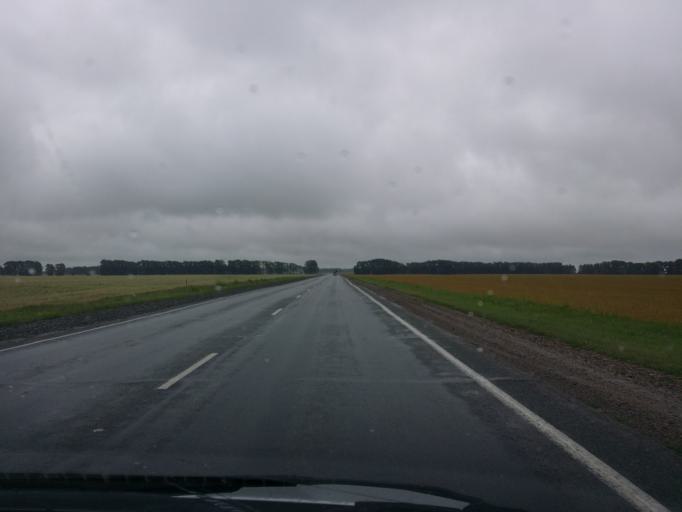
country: RU
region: Altai Krai
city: Bayunovskiye Klyuchi
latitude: 53.2832
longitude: 84.3405
